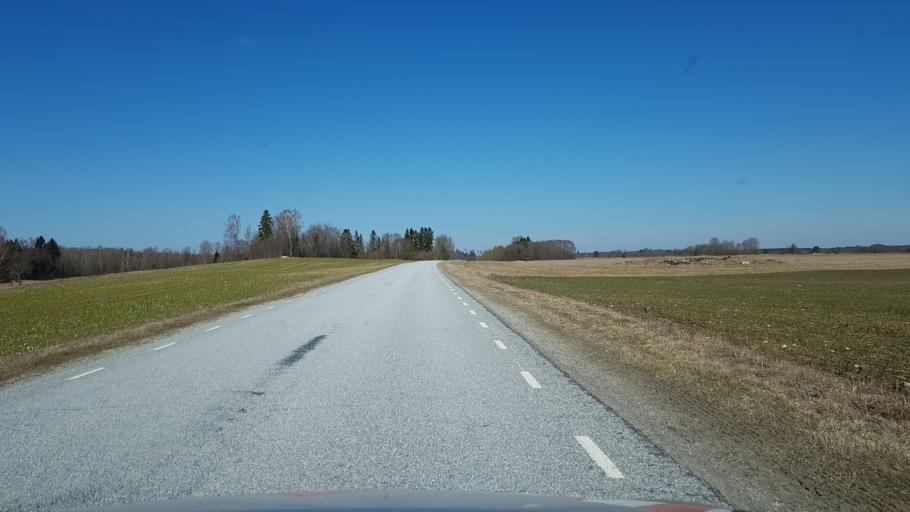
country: EE
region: Jaervamaa
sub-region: Koeru vald
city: Koeru
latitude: 59.0119
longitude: 26.0888
